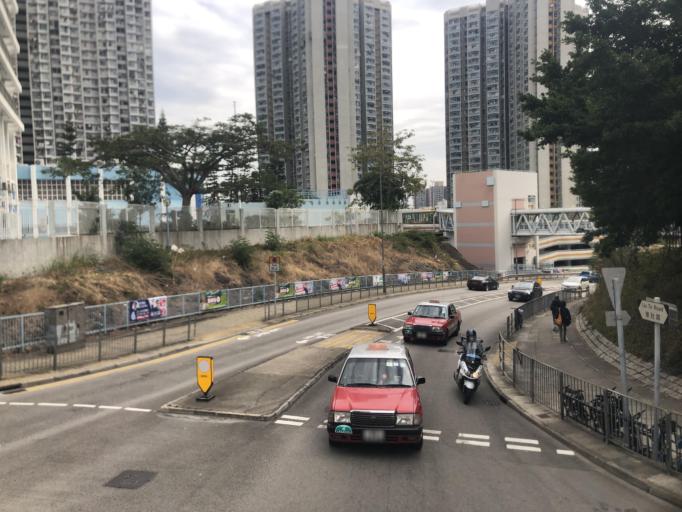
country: HK
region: Tsuen Wan
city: Tsuen Wan
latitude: 22.3572
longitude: 114.0969
